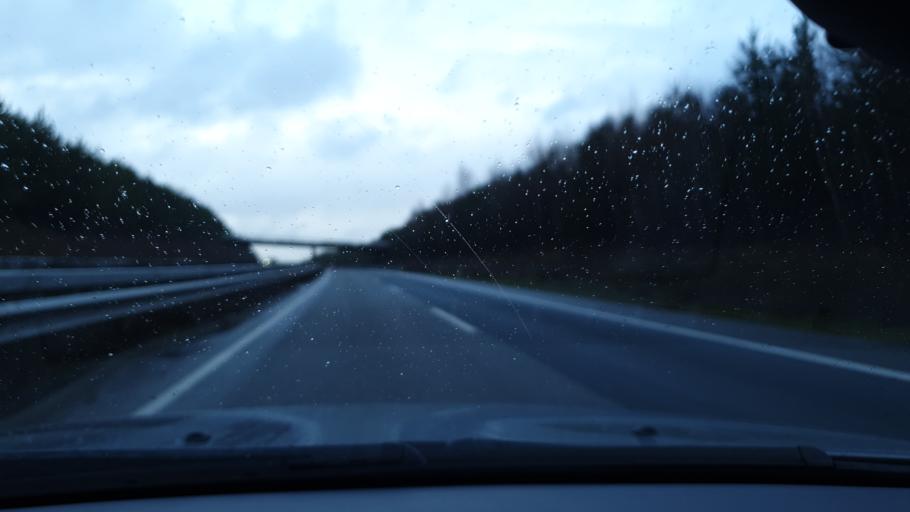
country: DE
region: Rheinland-Pfalz
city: Mehlingen
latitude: 49.4831
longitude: 7.8389
